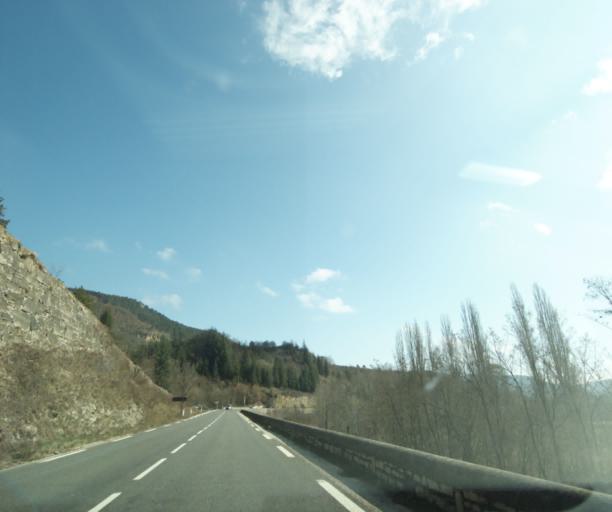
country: FR
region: Languedoc-Roussillon
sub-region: Departement de la Lozere
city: Chanac
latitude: 44.4843
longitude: 3.3088
